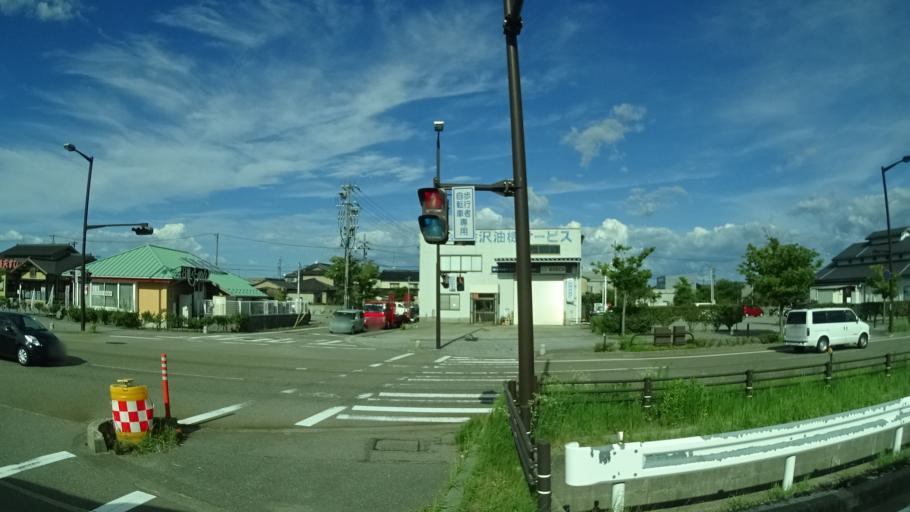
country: JP
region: Ishikawa
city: Kanazawa-shi
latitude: 36.6035
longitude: 136.6192
